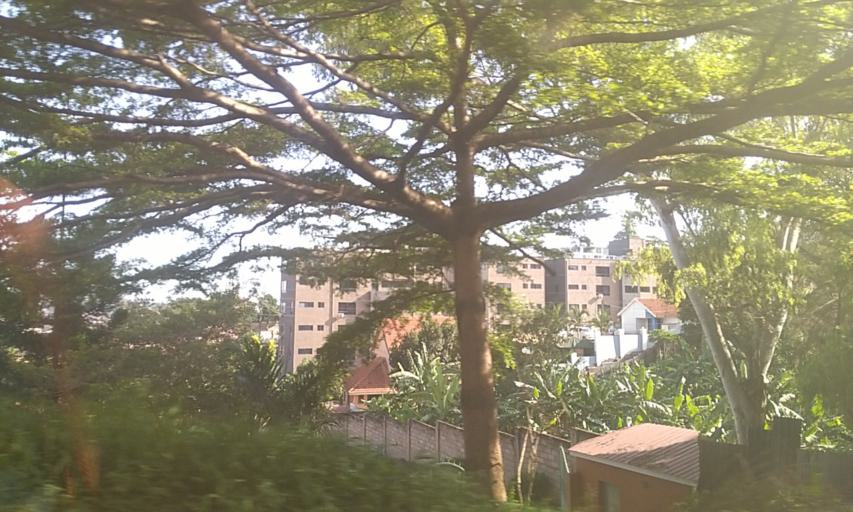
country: UG
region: Central Region
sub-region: Wakiso District
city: Kireka
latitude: 0.3526
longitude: 32.6077
